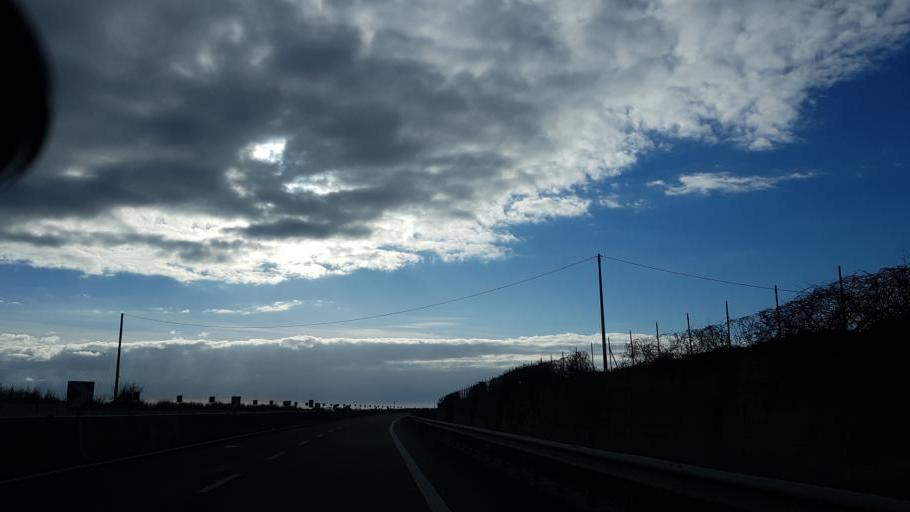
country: IT
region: Apulia
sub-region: Provincia di Brindisi
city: La Rosa
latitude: 40.5942
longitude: 17.9708
